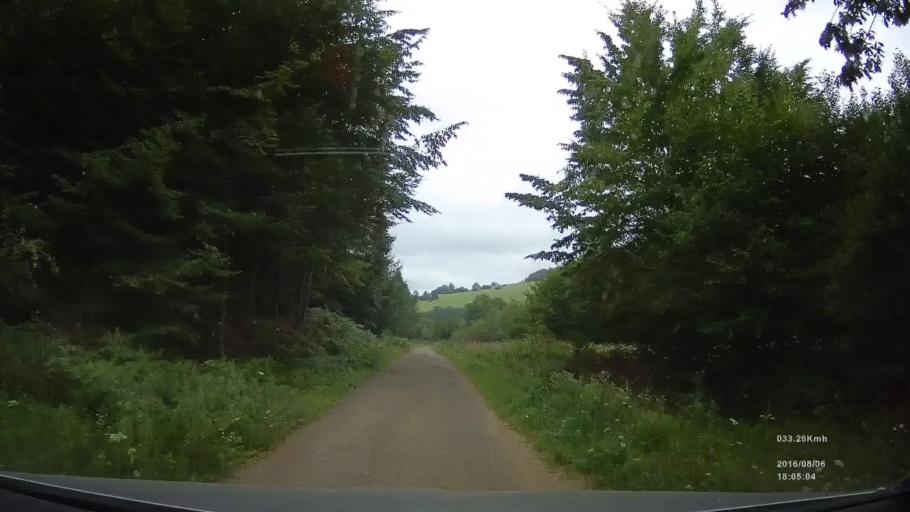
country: SK
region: Presovsky
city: Svidnik
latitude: 49.4094
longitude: 21.5678
